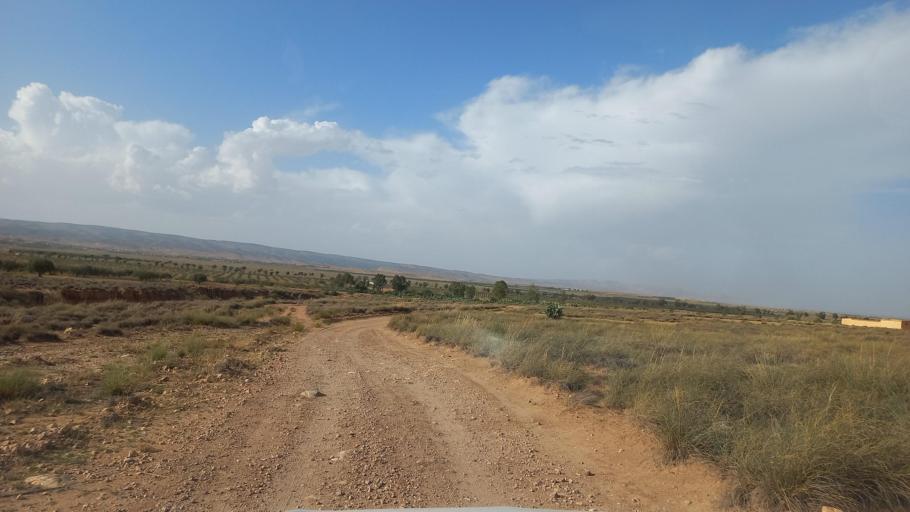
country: TN
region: Al Qasrayn
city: Kasserine
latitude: 35.2211
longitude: 8.9695
